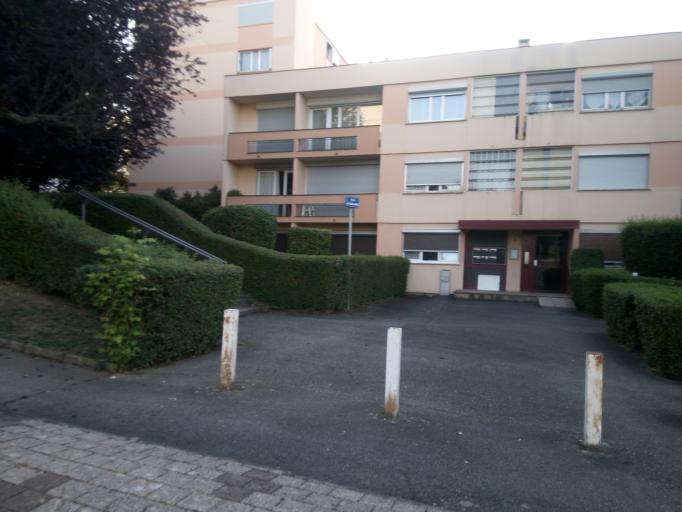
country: FR
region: Lorraine
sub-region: Departement de Meurthe-et-Moselle
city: Vandoeuvre-les-Nancy
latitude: 48.6637
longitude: 6.1718
